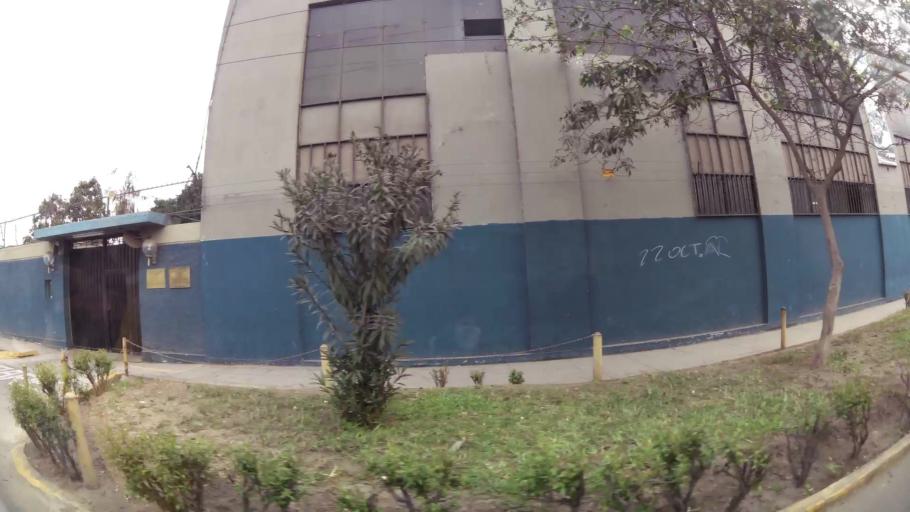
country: PE
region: Lima
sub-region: Lima
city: Surco
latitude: -12.1450
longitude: -77.0142
